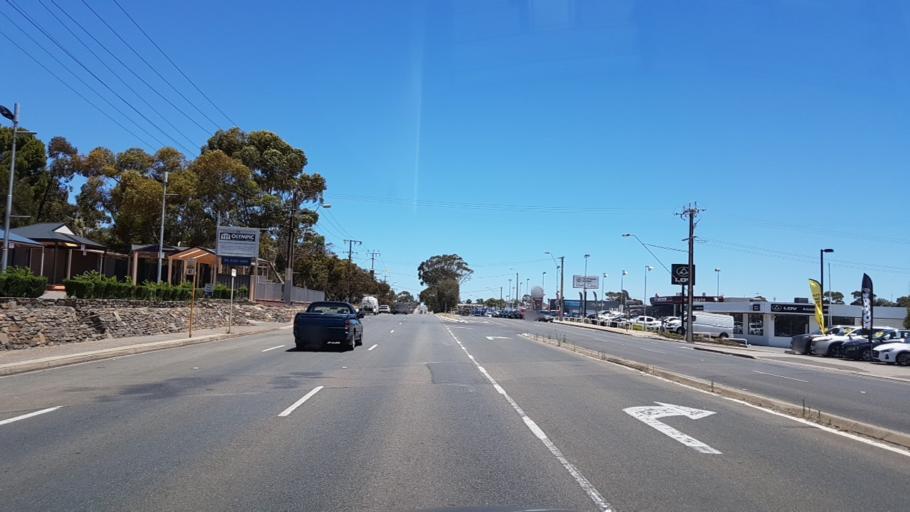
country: AU
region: South Australia
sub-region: Onkaparinga
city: Reynella
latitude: -35.1009
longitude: 138.5313
